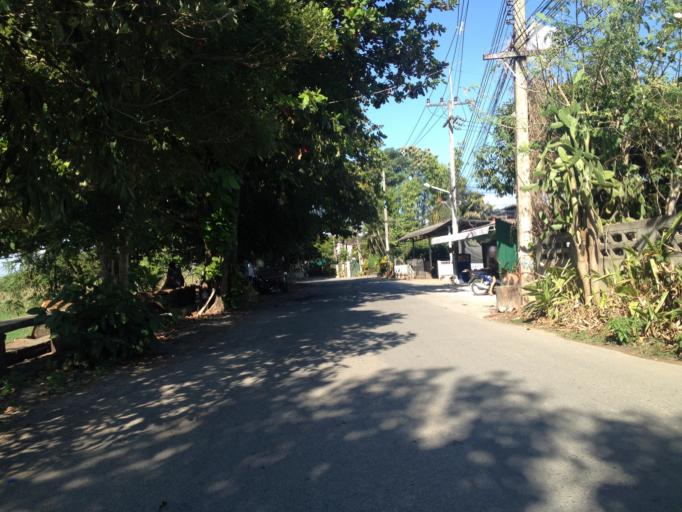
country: TH
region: Chiang Mai
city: Saraphi
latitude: 18.7154
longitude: 98.9871
